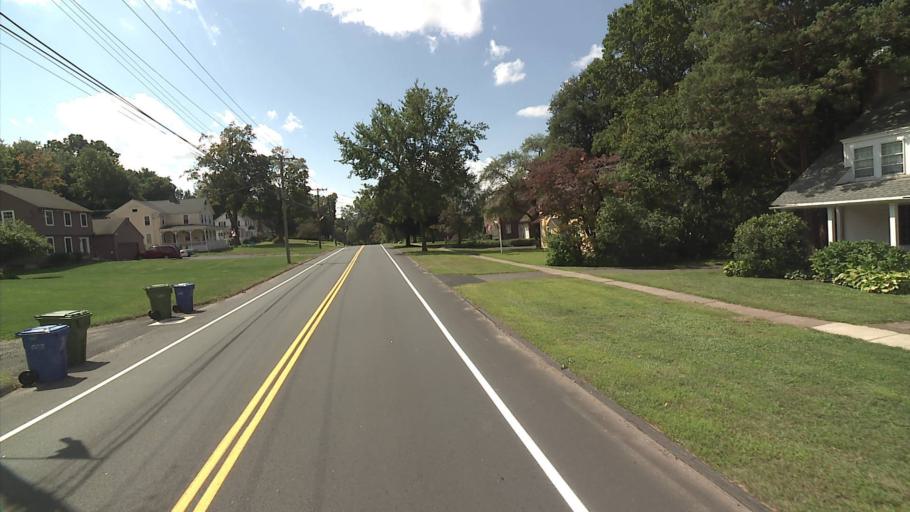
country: US
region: Connecticut
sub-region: Middlesex County
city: Cromwell
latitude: 41.5877
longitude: -72.6280
